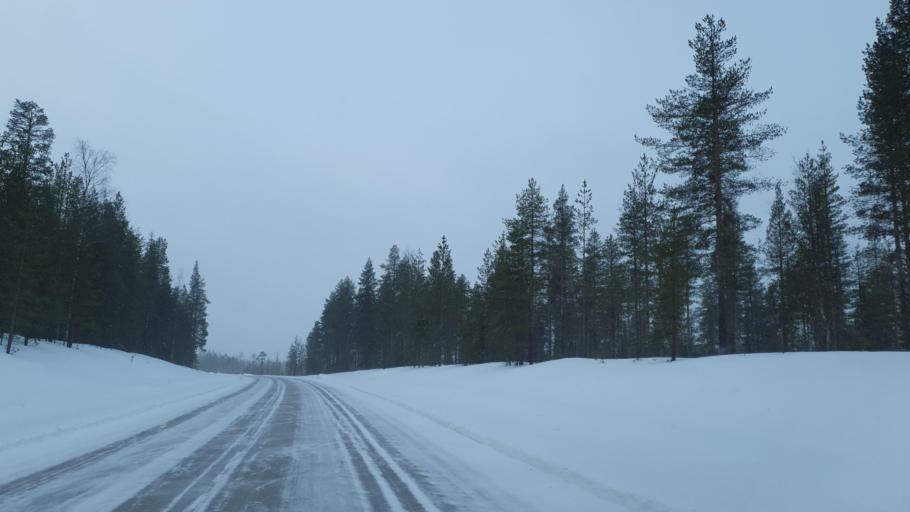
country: FI
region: Lapland
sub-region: Tunturi-Lappi
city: Kolari
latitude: 67.4557
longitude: 23.8457
